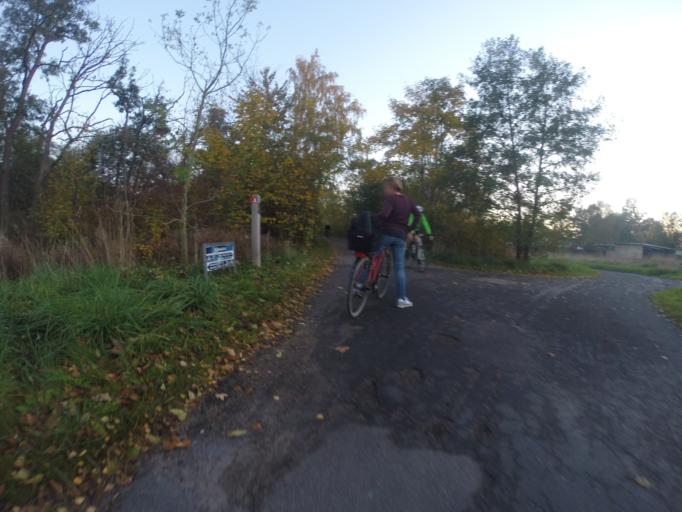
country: DK
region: Capital Region
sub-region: Hoje-Taastrup Kommune
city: Taastrup
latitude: 55.6610
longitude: 12.3224
